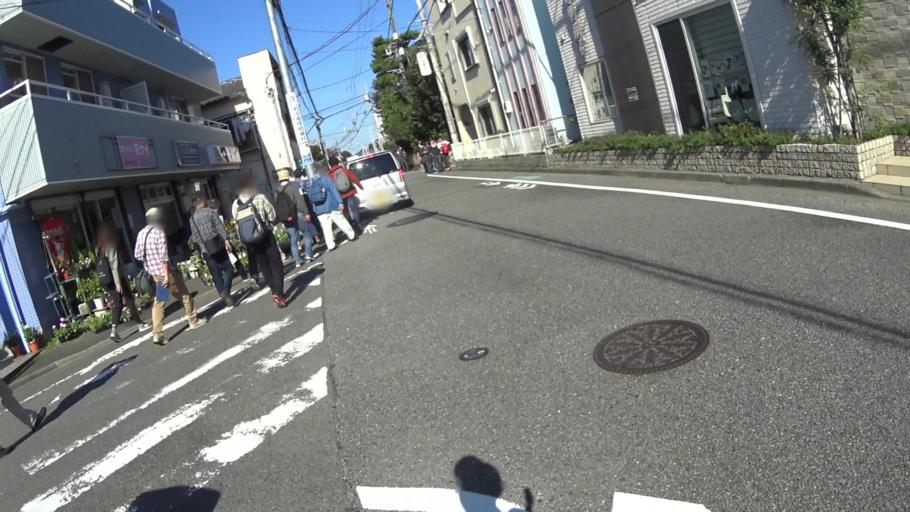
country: JP
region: Tokyo
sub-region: Machida-shi
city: Machida
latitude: 35.5536
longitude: 139.4485
